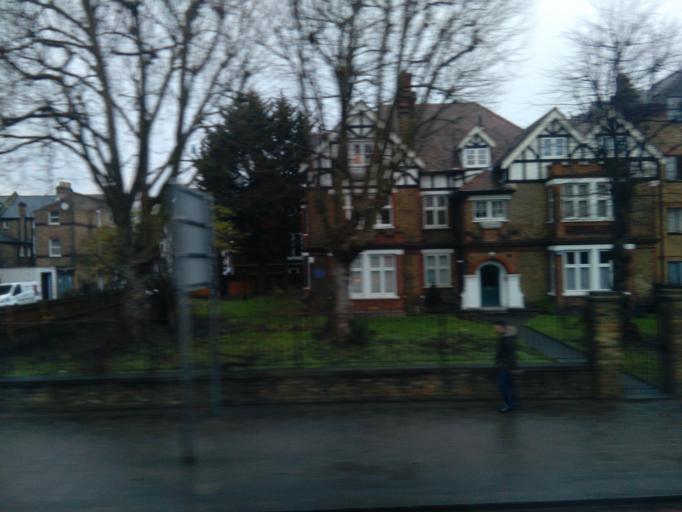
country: GB
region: England
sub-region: Greater London
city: Battersea
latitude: 51.4612
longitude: -0.1587
